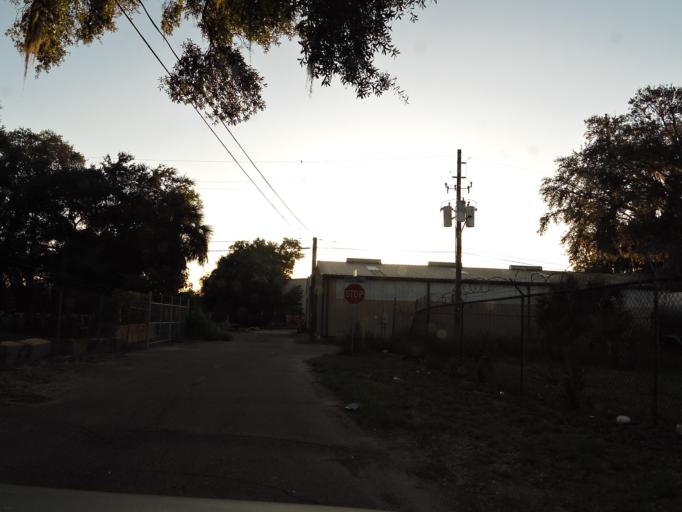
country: US
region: Florida
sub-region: Duval County
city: Jacksonville
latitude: 30.3564
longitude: -81.6283
